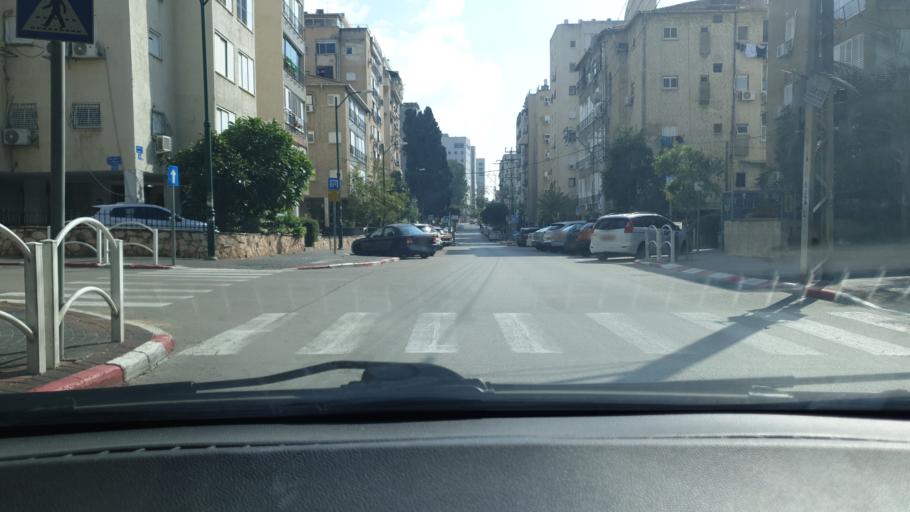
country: IL
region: Central District
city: Rishon LeZiyyon
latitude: 31.9668
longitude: 34.8047
